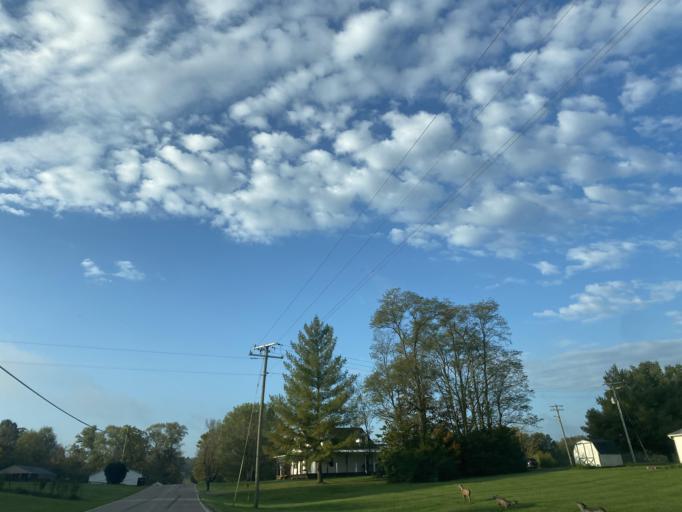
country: US
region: Kentucky
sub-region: Pendleton County
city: Falmouth
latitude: 38.7757
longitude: -84.3353
